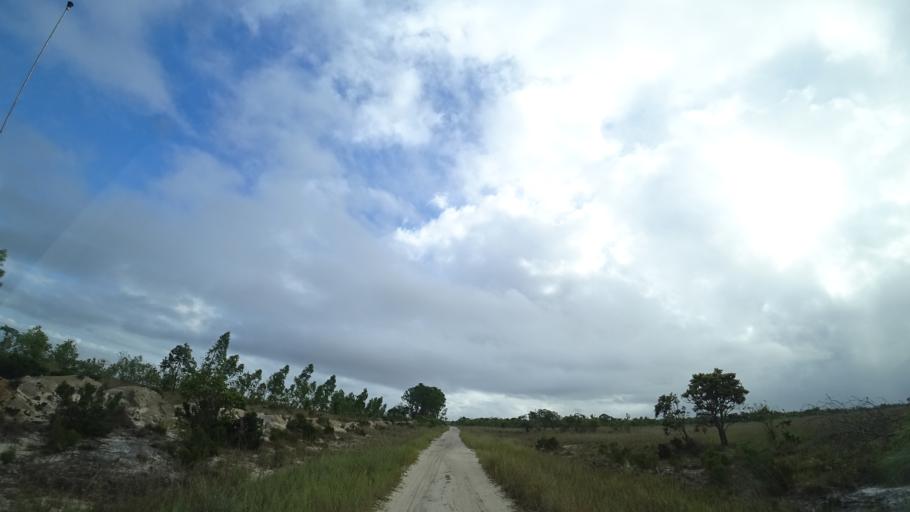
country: MZ
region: Sofala
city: Beira
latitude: -19.6239
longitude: 35.0605
